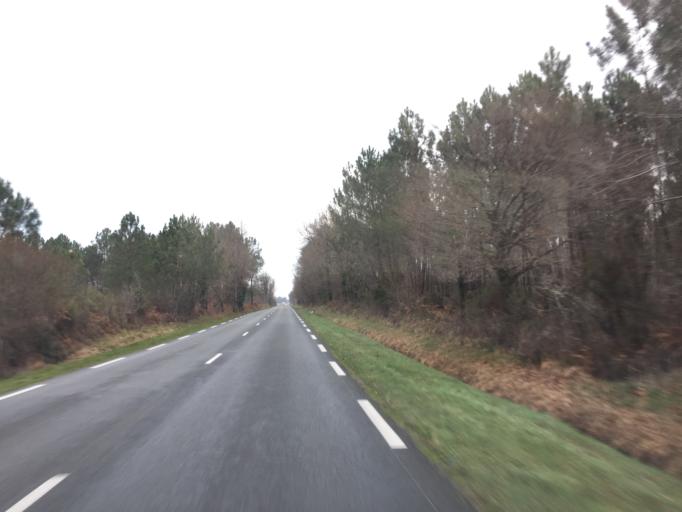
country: FR
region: Aquitaine
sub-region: Departement de la Gironde
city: Saint-Sauveur
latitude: 45.1914
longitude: -0.8519
